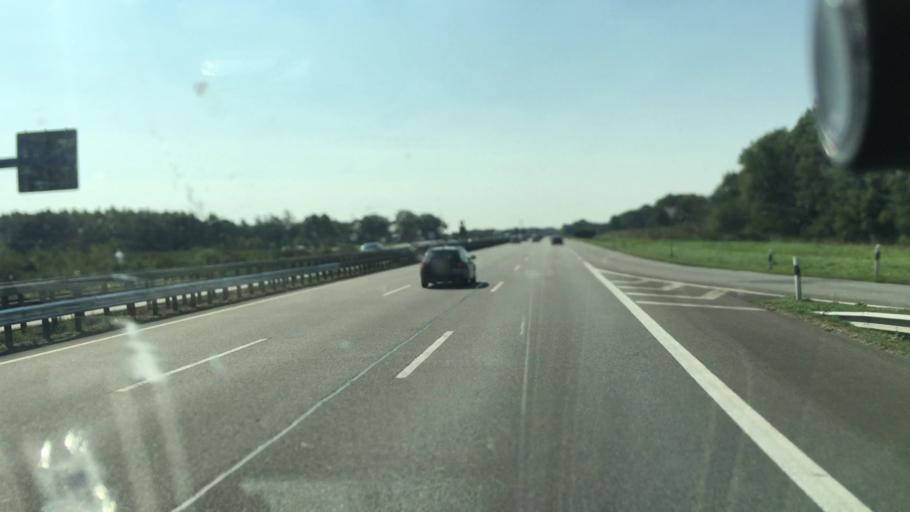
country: DE
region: Lower Saxony
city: Bakum
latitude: 52.7130
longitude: 8.1727
